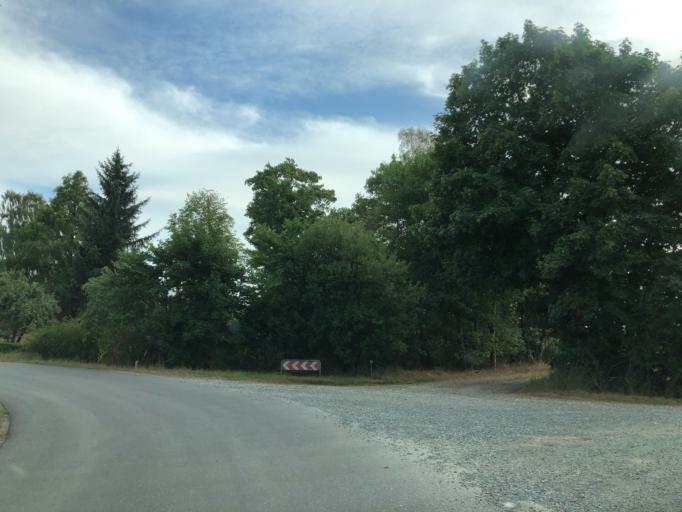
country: DK
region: South Denmark
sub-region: Vejle Kommune
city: Egtved
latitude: 55.6856
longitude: 9.2622
